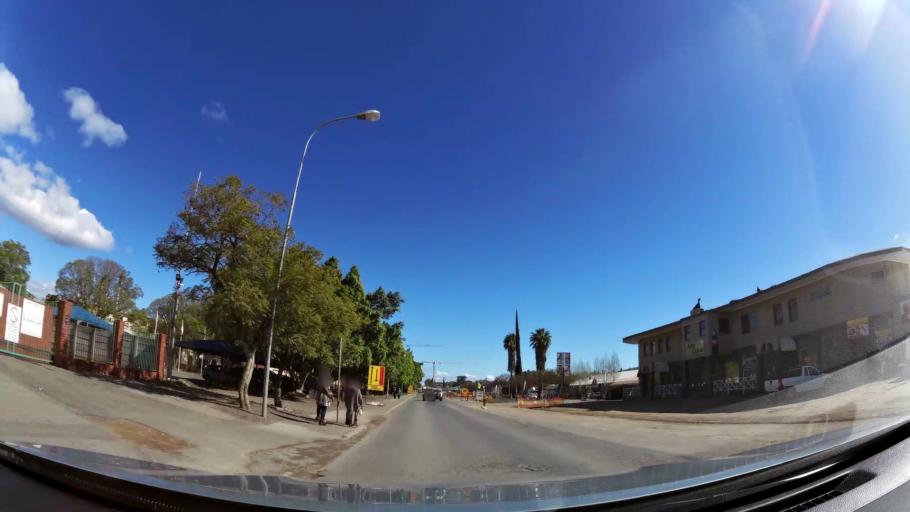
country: ZA
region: Western Cape
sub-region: Cape Winelands District Municipality
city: Ashton
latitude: -33.8329
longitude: 20.0656
